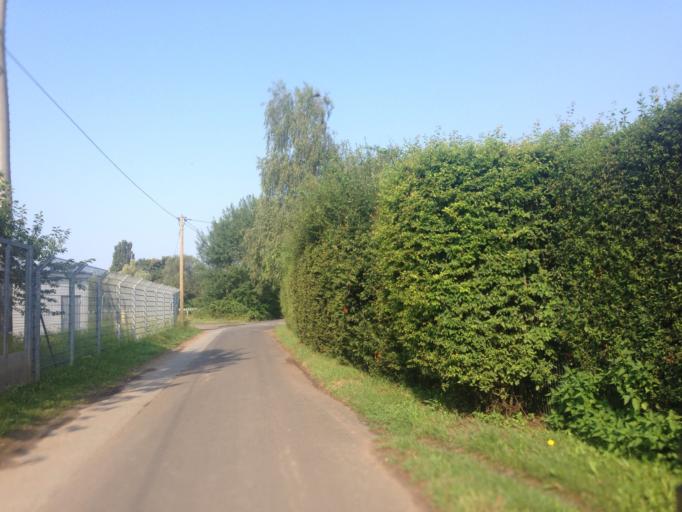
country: DE
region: Hesse
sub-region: Regierungsbezirk Darmstadt
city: Maintal
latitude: 50.1364
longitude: 8.8240
